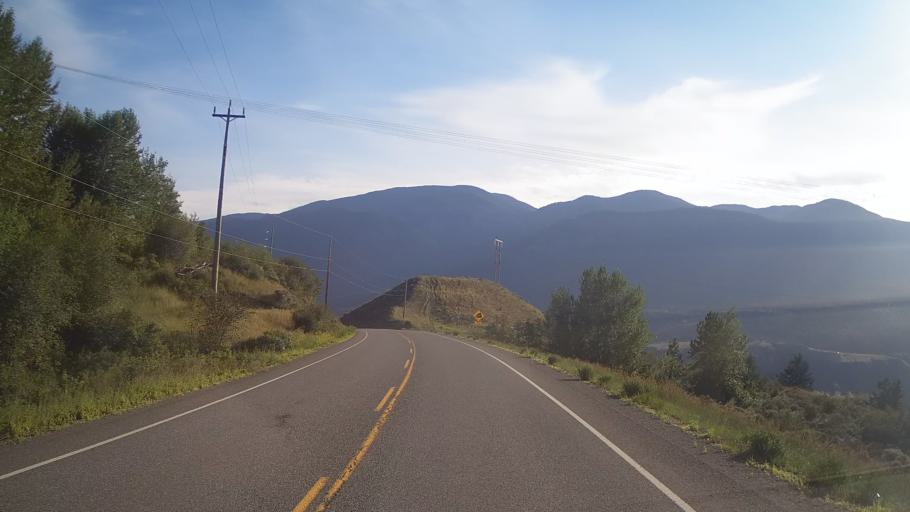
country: CA
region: British Columbia
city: Lillooet
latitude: 50.8657
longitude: -121.8501
